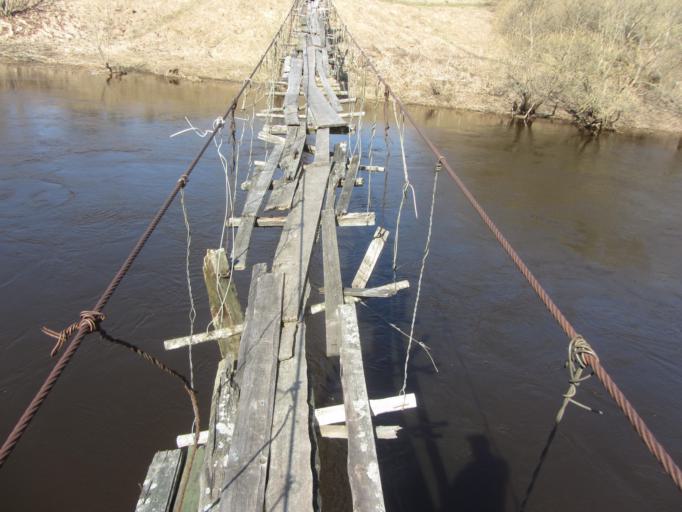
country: LT
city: Nemencine
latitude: 54.8699
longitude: 25.5725
